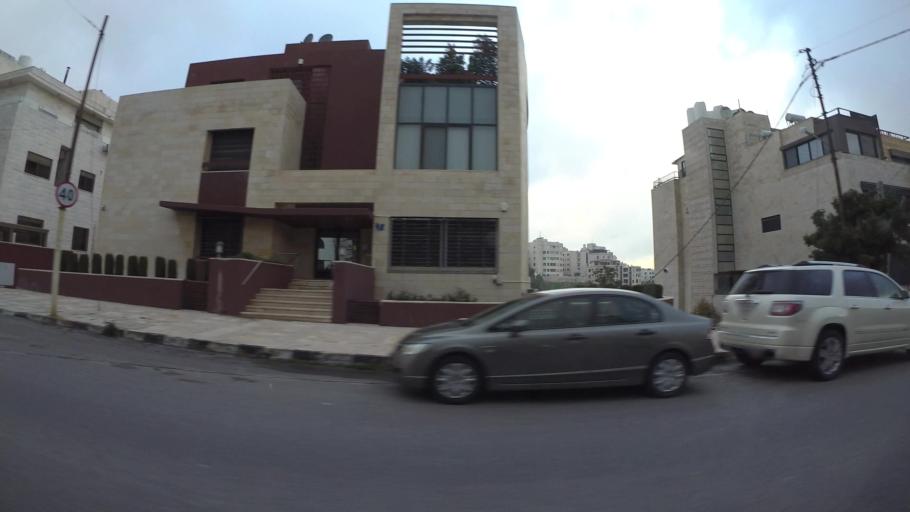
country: JO
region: Amman
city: Amman
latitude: 31.9514
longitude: 35.8913
